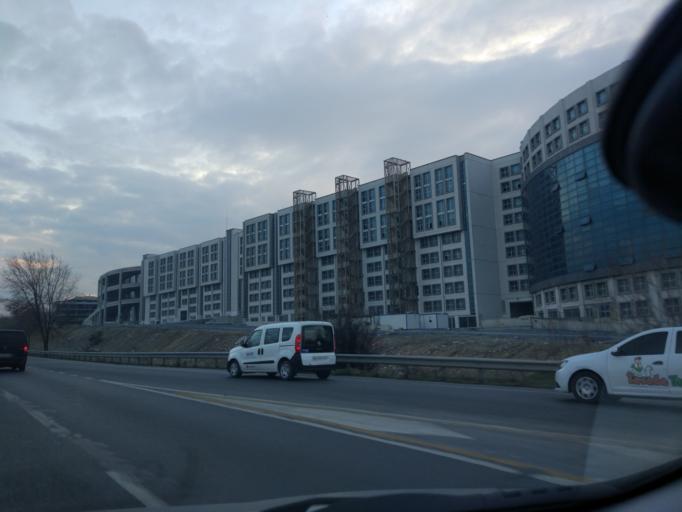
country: TR
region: Istanbul
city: Yakuplu
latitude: 41.0038
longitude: 28.6775
